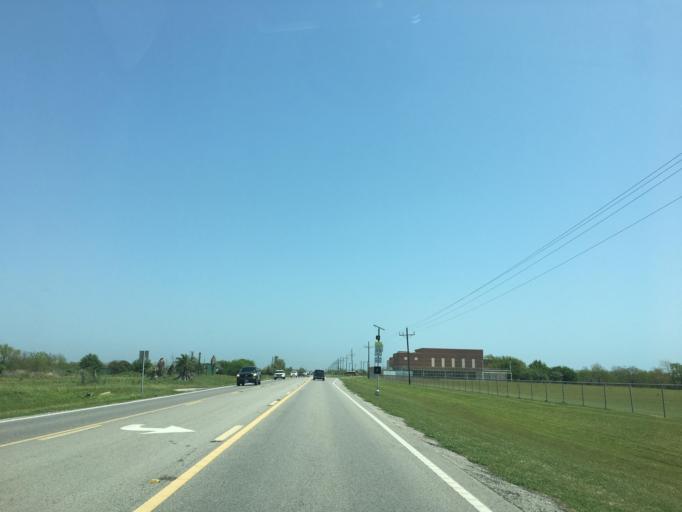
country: US
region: Texas
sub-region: Galveston County
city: Bolivar Peninsula
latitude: 29.4265
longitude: -94.6931
